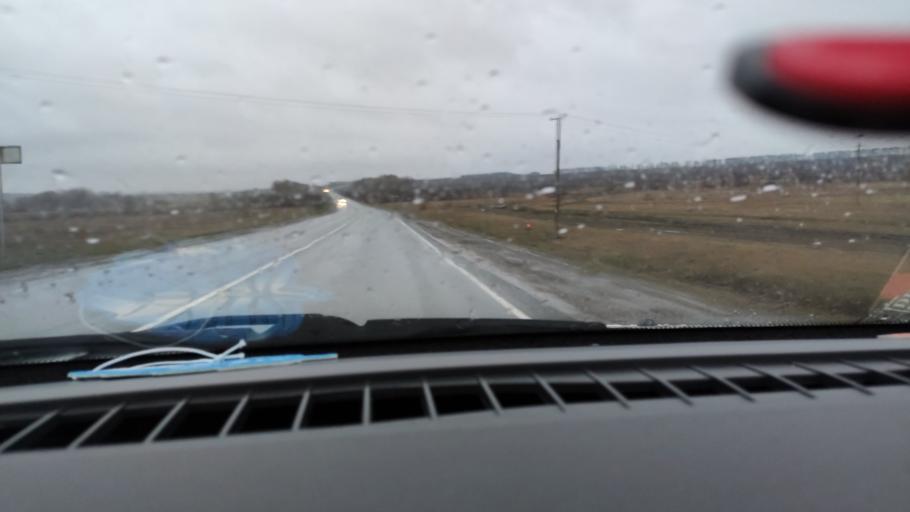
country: RU
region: Tatarstan
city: Mendeleyevsk
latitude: 55.9696
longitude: 52.3176
